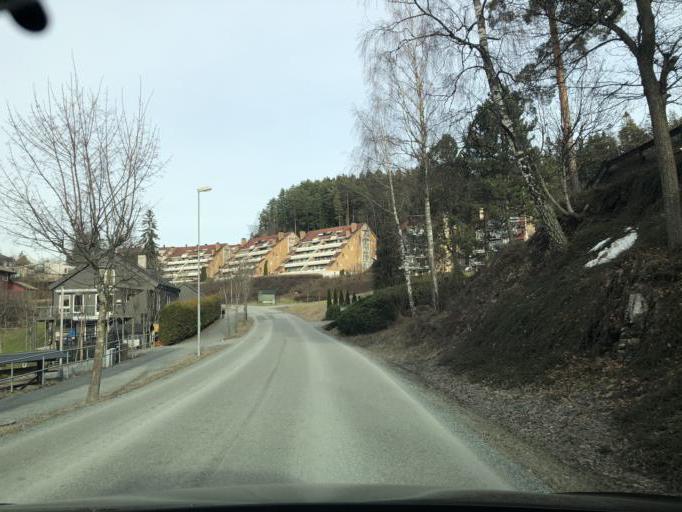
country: NO
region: Akershus
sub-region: Baerum
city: Sandvika
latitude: 59.8651
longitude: 10.5138
